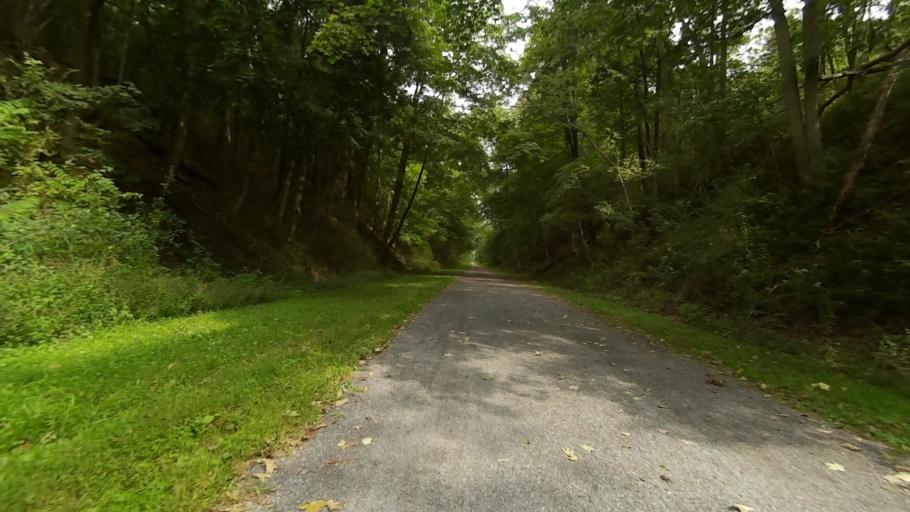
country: US
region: Pennsylvania
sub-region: Blair County
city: Williamsburg
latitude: 40.5262
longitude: -78.1703
